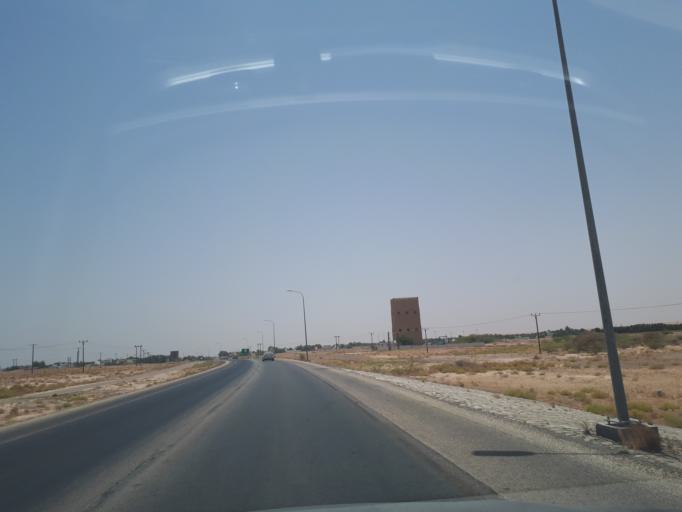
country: OM
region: Ash Sharqiyah
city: Al Qabil
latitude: 22.5108
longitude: 58.7400
